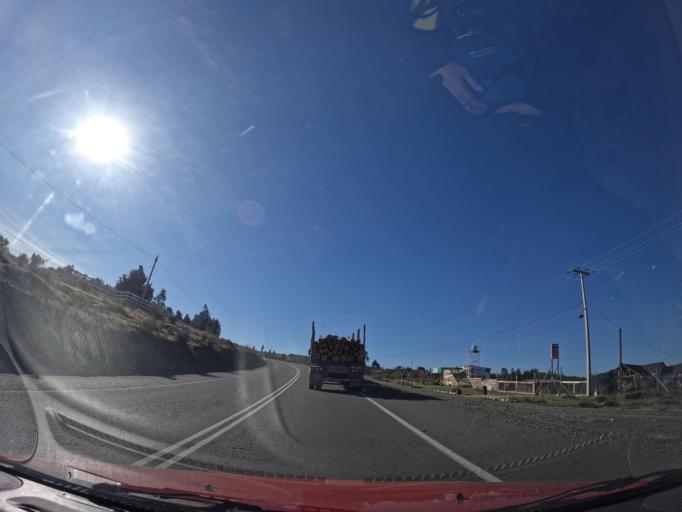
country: CL
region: Maule
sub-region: Provincia de Cauquenes
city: Cauquenes
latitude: -35.9413
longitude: -72.1970
